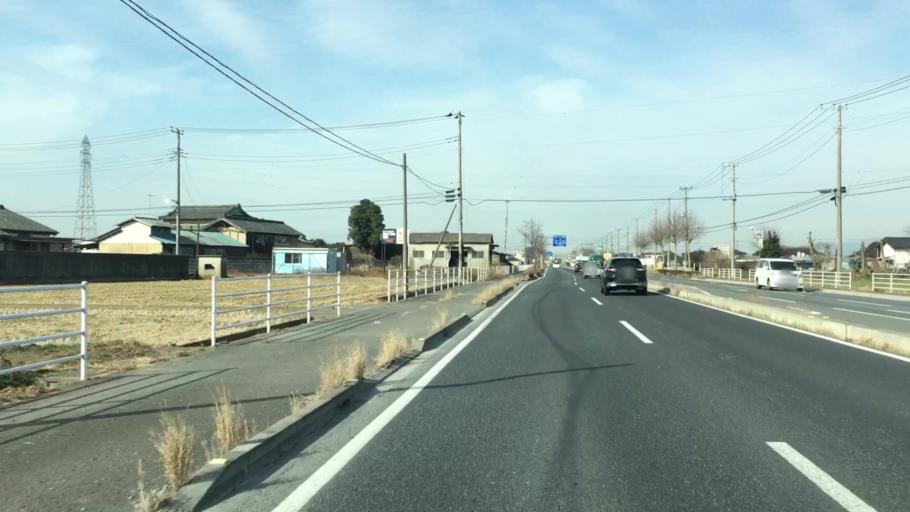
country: JP
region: Gunma
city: Tatebayashi
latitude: 36.2326
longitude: 139.4847
